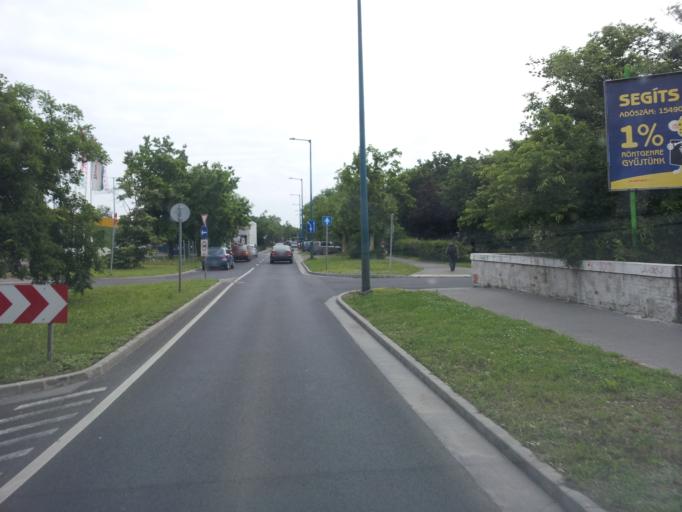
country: HU
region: Budapest
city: Budapest XIV. keruelet
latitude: 47.5326
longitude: 19.1022
